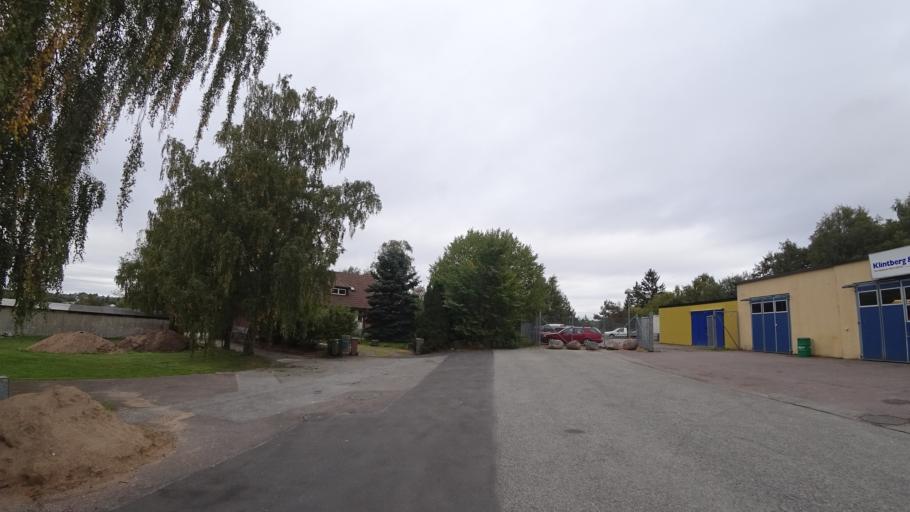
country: SE
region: Skane
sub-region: Kavlinge Kommun
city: Kaevlinge
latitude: 55.7813
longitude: 13.1077
